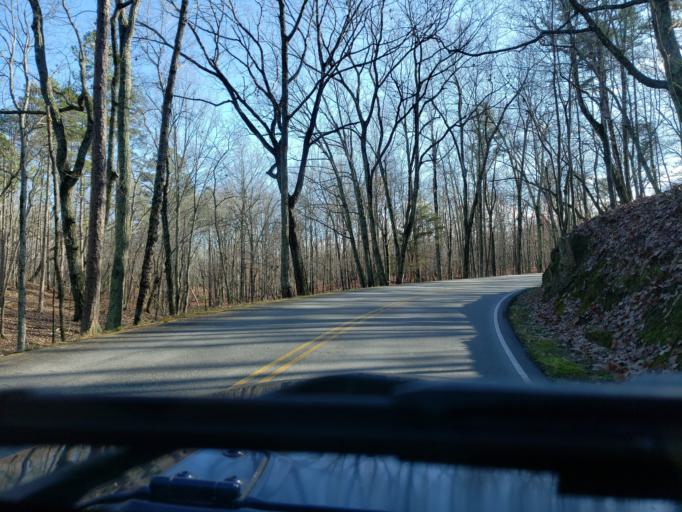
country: US
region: North Carolina
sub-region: Cleveland County
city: White Plains
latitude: 35.1474
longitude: -81.3877
